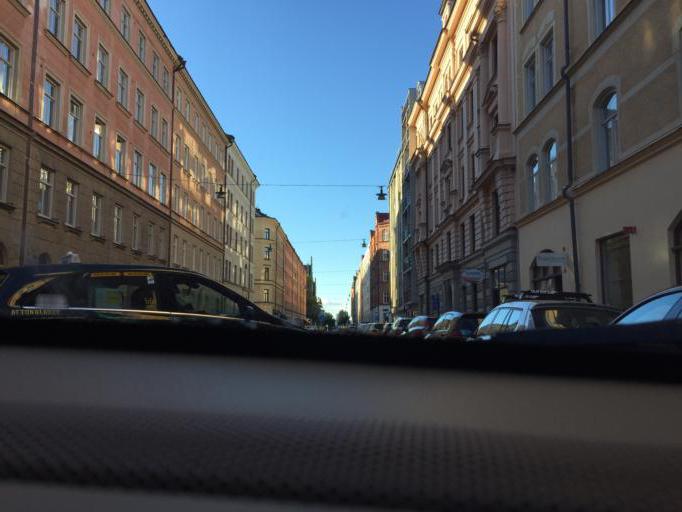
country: SE
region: Stockholm
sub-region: Stockholms Kommun
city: Stockholm
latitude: 59.3485
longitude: 18.0580
